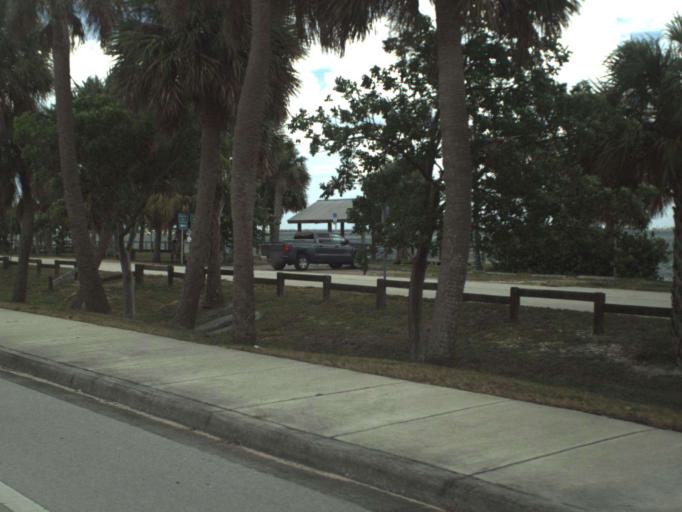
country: US
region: Florida
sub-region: Martin County
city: Jensen Beach
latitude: 27.2516
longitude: -80.2248
